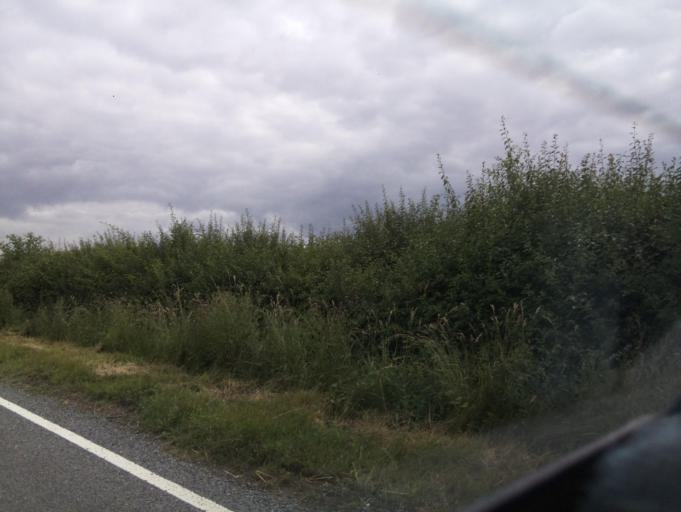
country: GB
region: England
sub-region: District of Rutland
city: Ryhall
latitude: 52.6883
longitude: -0.4853
